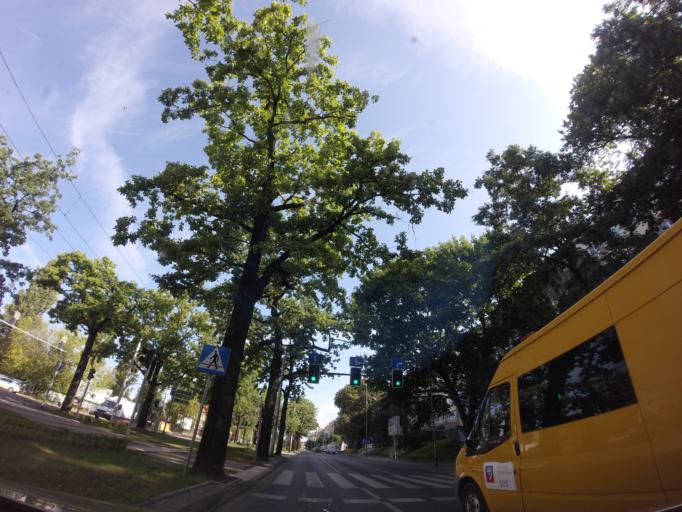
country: PL
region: West Pomeranian Voivodeship
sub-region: Szczecin
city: Szczecin
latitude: 53.4212
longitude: 14.5346
